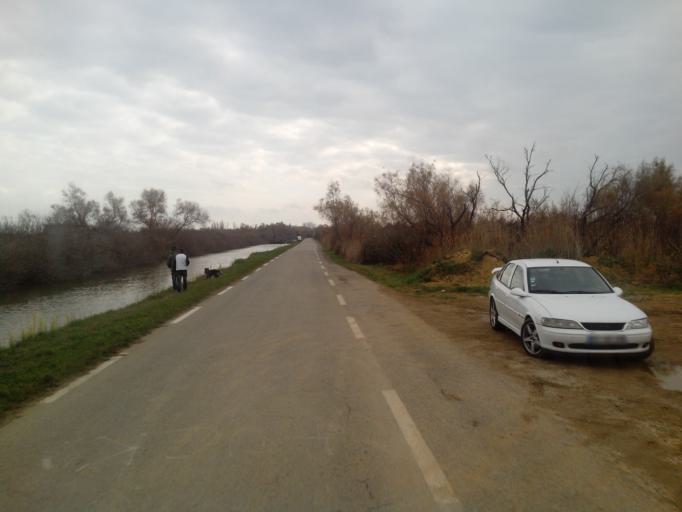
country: FR
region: Languedoc-Roussillon
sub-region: Departement du Gard
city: Vauvert
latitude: 43.6098
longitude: 4.3317
